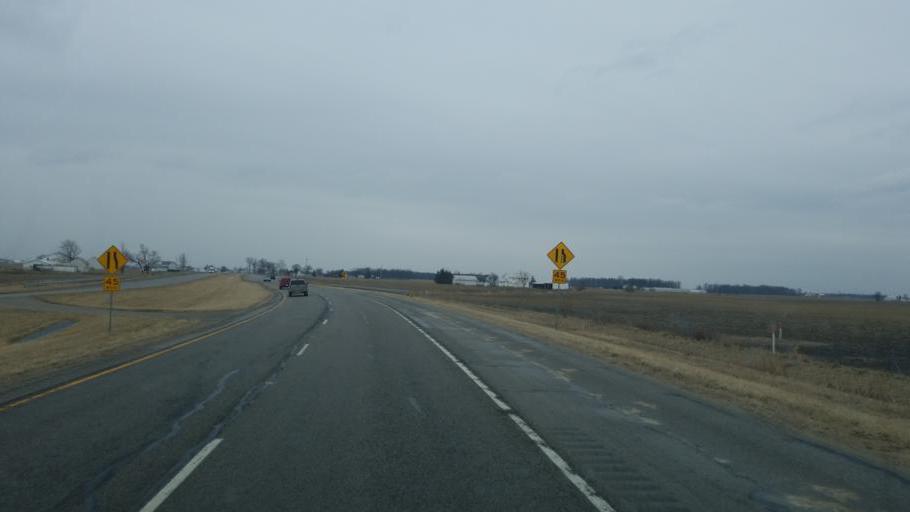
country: US
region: Indiana
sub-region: Adams County
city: Berne
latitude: 40.7420
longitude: -84.9559
